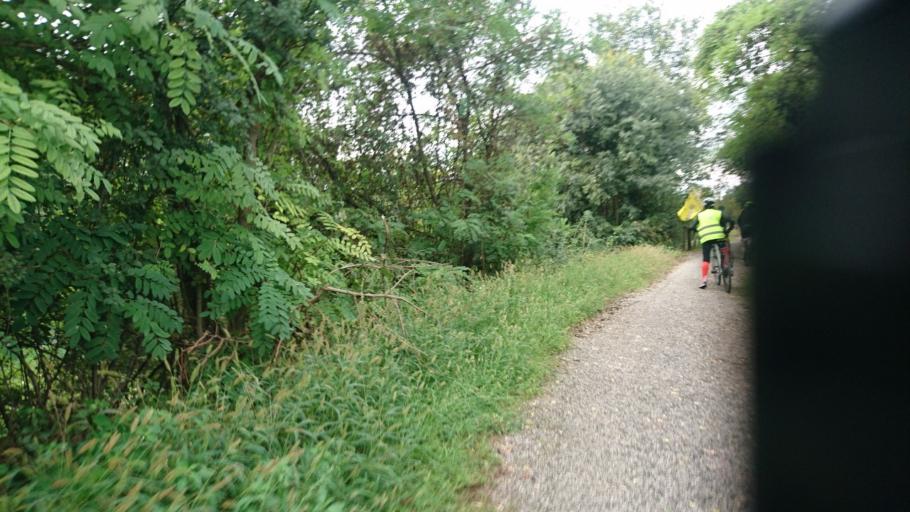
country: IT
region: Veneto
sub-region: Provincia di Vicenza
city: Montebello Vicentino
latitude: 45.4688
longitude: 11.3881
